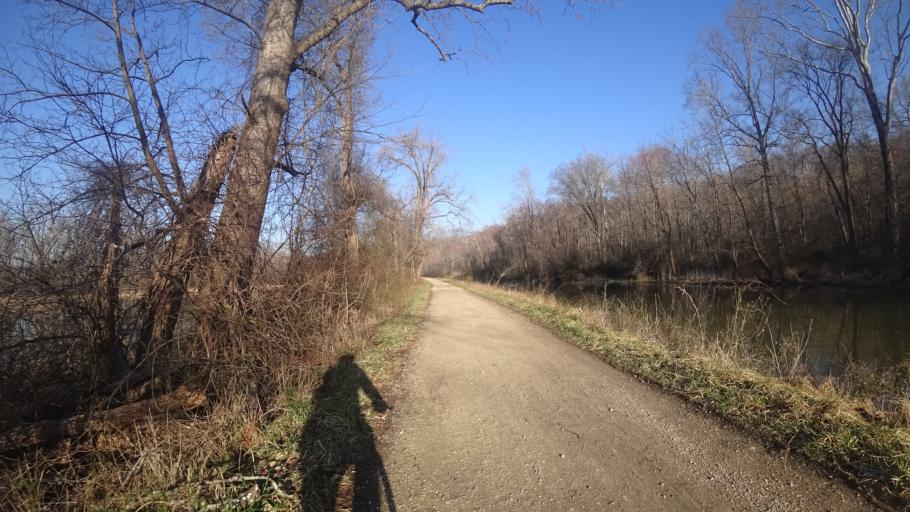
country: US
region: Maryland
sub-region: Montgomery County
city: Travilah
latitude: 39.0582
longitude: -77.2996
